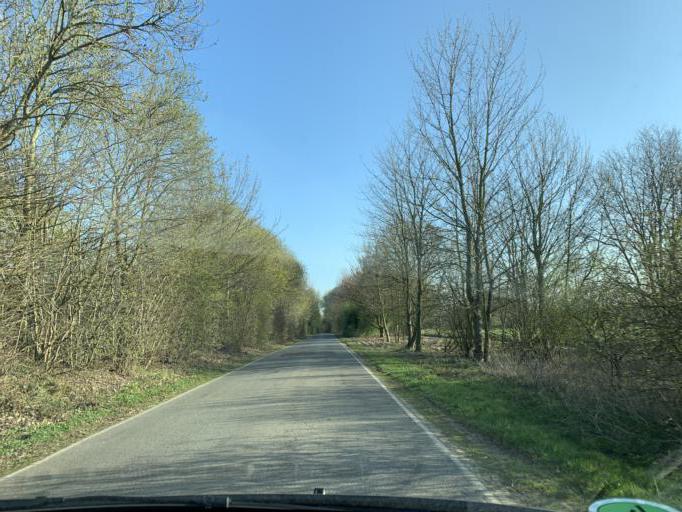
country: DE
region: North Rhine-Westphalia
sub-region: Regierungsbezirk Koln
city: Titz
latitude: 51.0899
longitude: 6.4041
